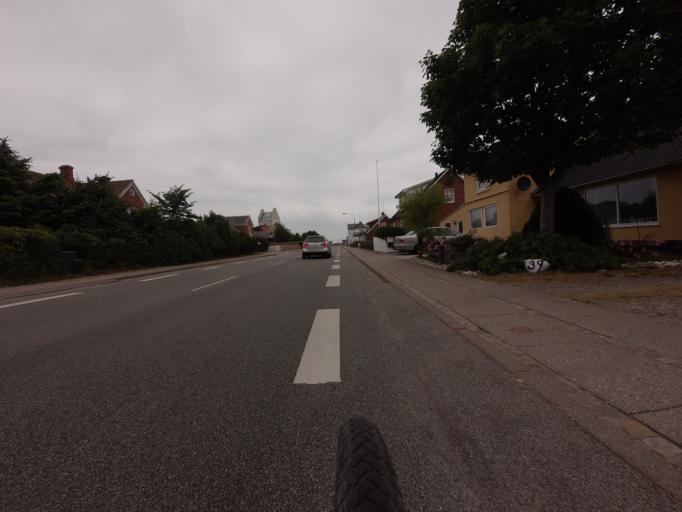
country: DK
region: North Denmark
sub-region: Laeso Kommune
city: Byrum
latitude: 57.2902
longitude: 10.9235
